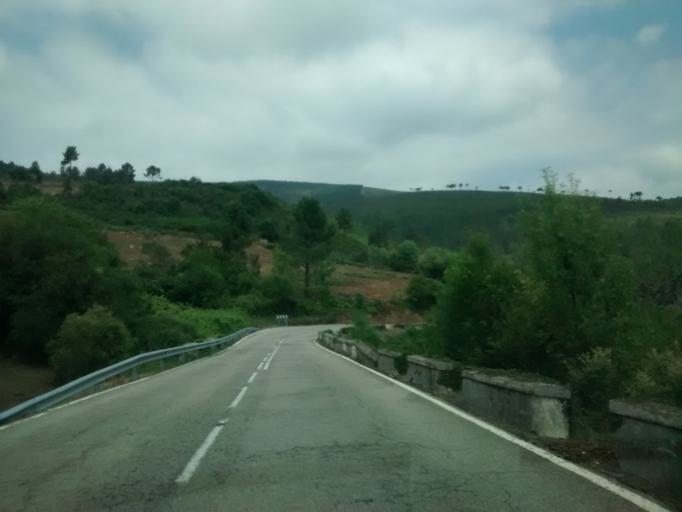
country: ES
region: Galicia
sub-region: Provincia de Ourense
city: Manzaneda
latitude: 42.3416
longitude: -7.1777
